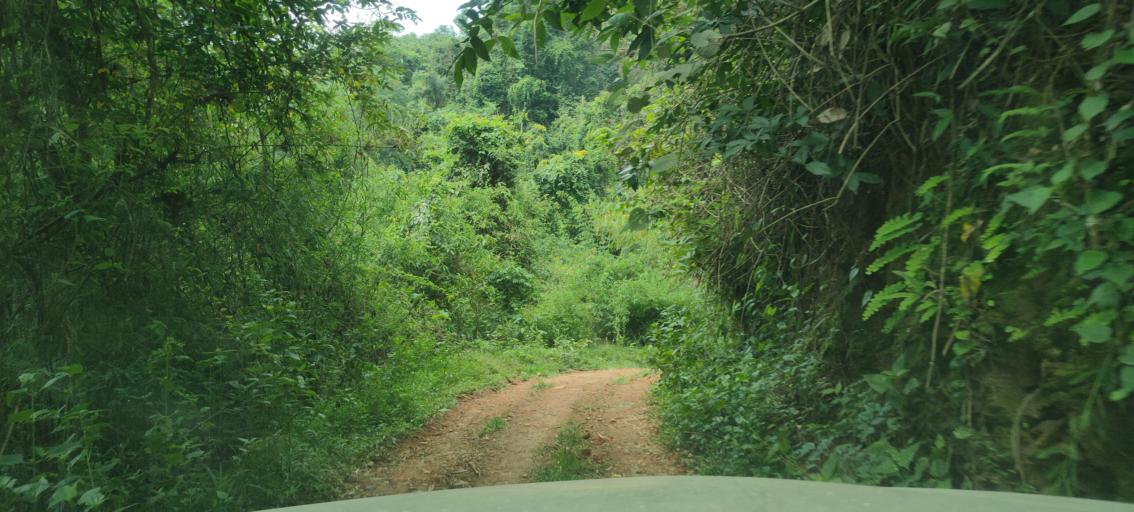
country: LA
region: Loungnamtha
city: Muang Nale
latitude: 20.4204
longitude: 101.4643
